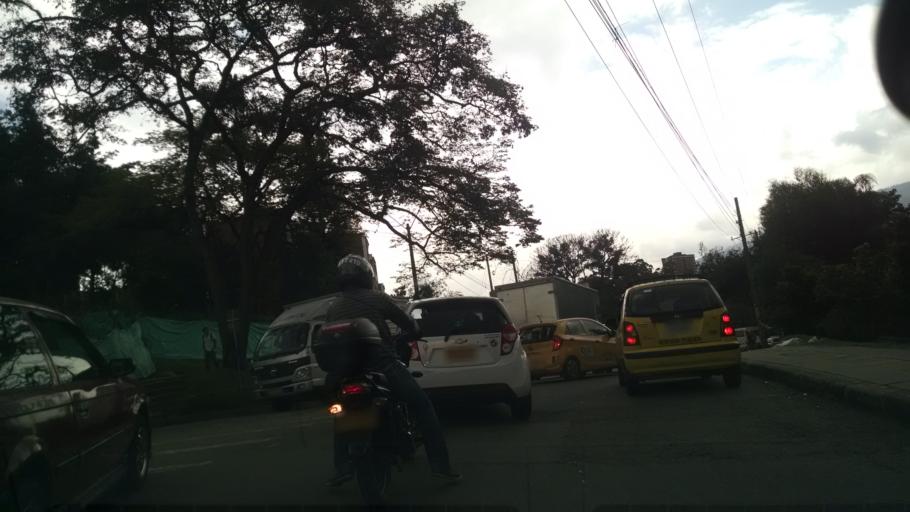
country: CO
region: Antioquia
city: Medellin
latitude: 6.2724
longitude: -75.5905
